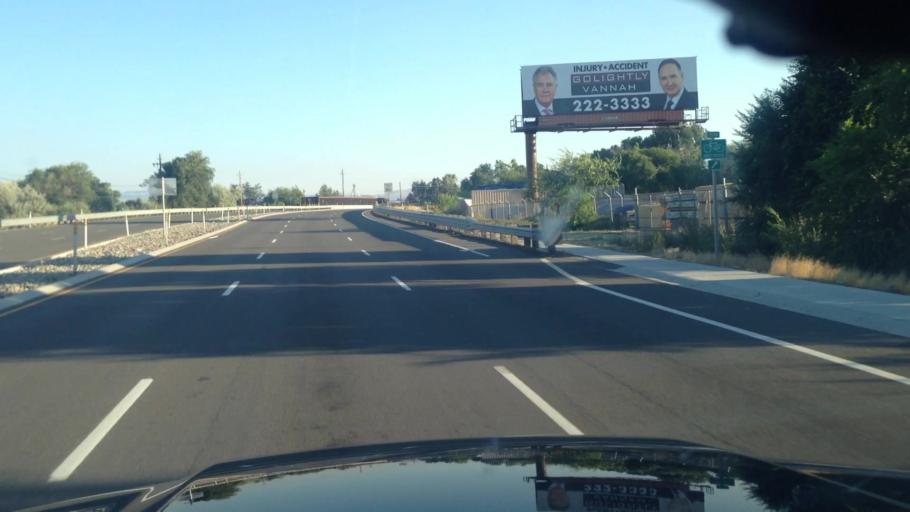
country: US
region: Nevada
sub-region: Washoe County
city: Sparks
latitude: 39.5198
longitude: -119.7404
